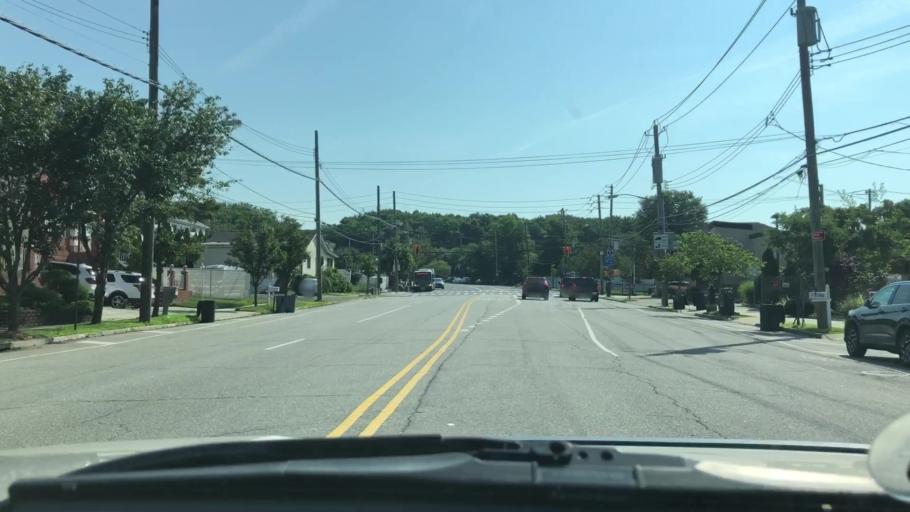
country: US
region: New Jersey
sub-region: Middlesex County
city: Carteret
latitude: 40.5189
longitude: -74.1982
